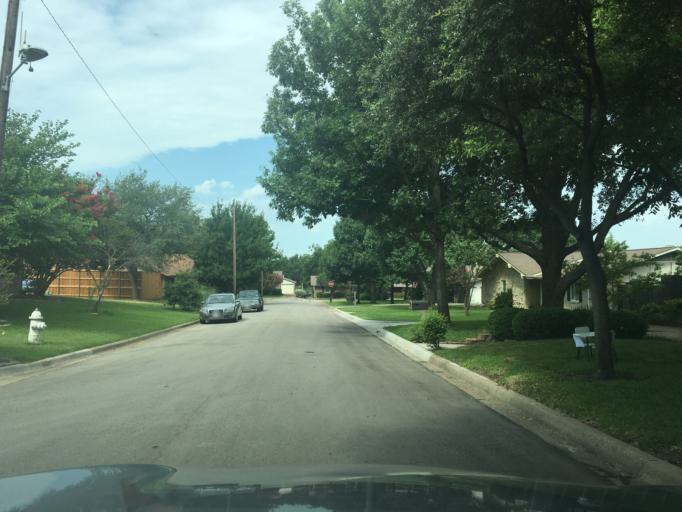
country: US
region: Texas
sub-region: Dallas County
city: Addison
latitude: 32.9444
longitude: -96.8569
